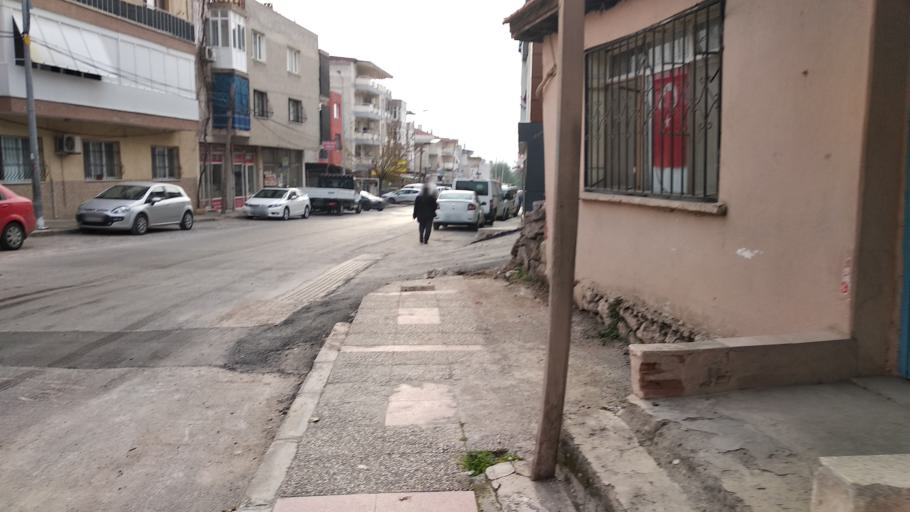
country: TR
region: Izmir
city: Karsiyaka
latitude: 38.4941
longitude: 27.0742
